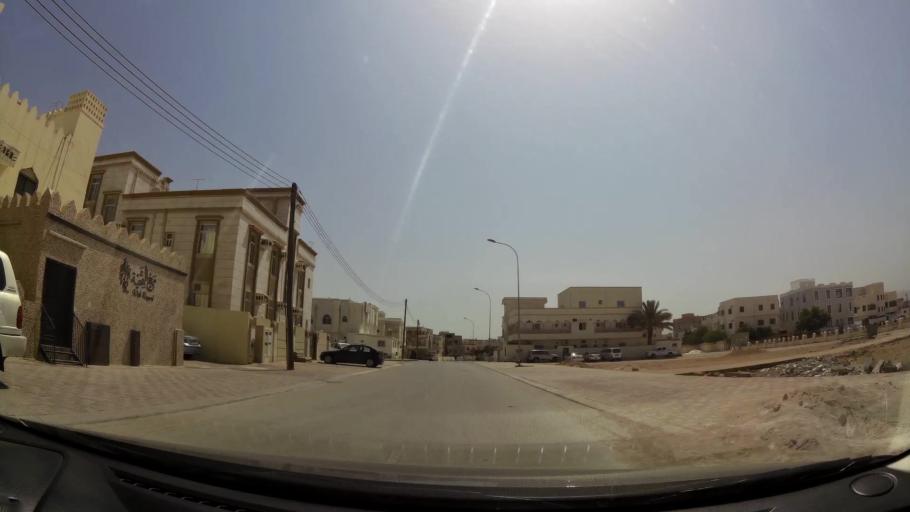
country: OM
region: Zufar
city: Salalah
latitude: 17.0183
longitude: 54.0703
